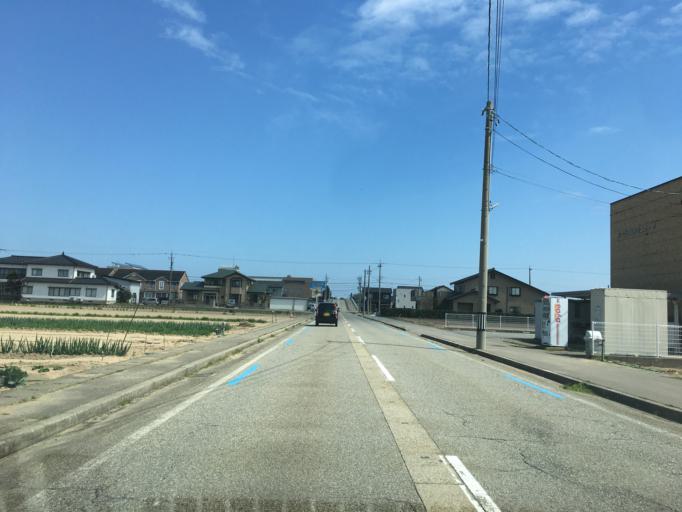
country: JP
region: Toyama
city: Himi
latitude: 36.8307
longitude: 137.0041
